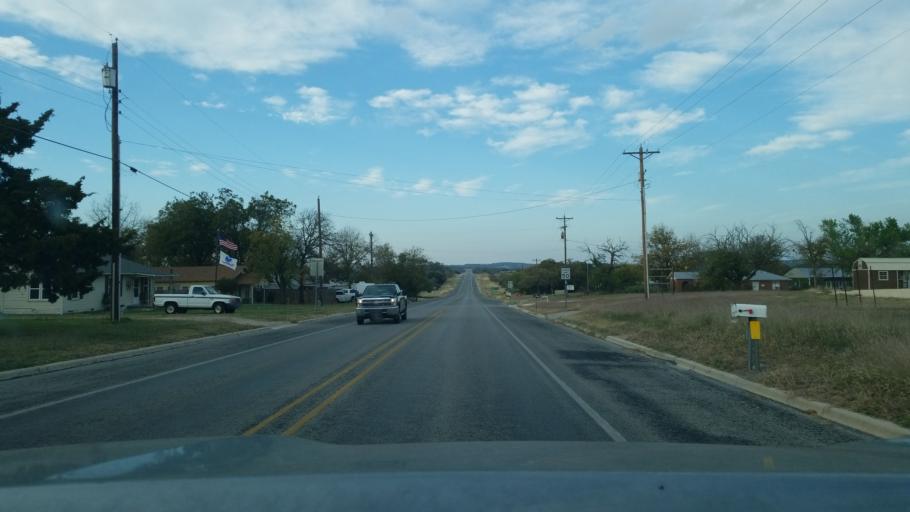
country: US
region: Texas
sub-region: Brown County
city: Lake Brownwood
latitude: 31.9813
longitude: -98.9206
